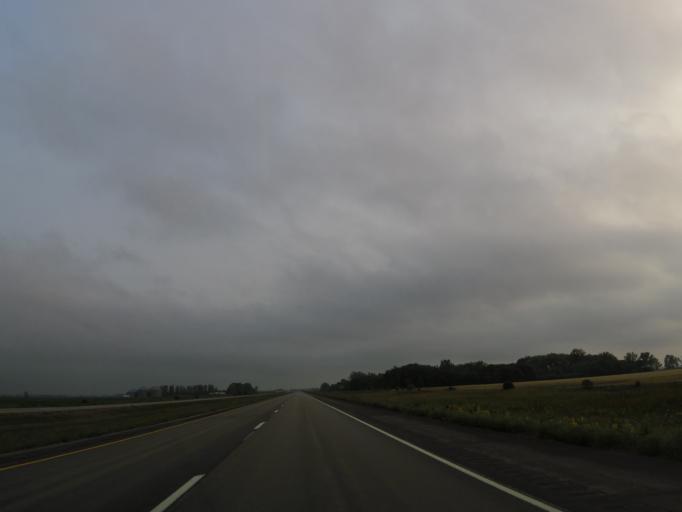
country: US
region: North Dakota
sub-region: Walsh County
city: Grafton
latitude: 48.5412
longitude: -97.1860
